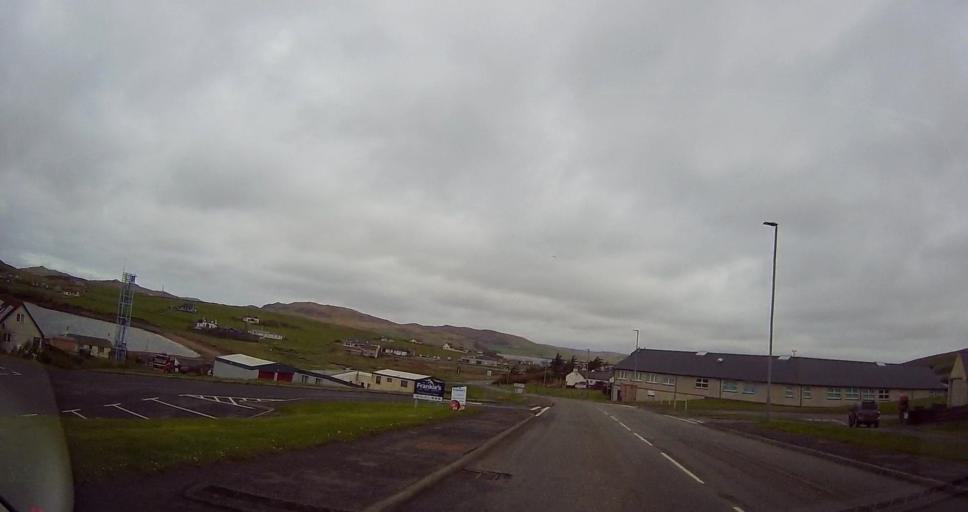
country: GB
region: Scotland
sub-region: Shetland Islands
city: Lerwick
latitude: 60.3929
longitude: -1.3501
